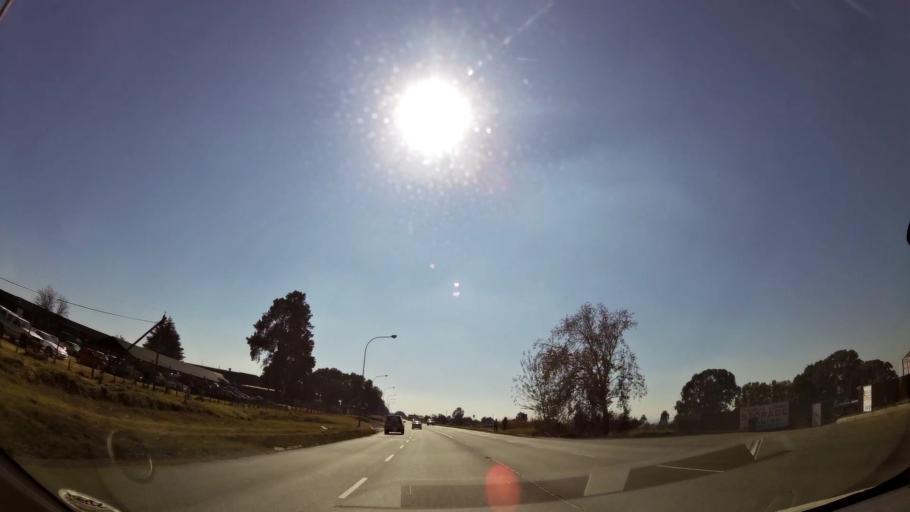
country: ZA
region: Mpumalanga
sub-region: Nkangala District Municipality
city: Witbank
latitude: -25.8552
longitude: 29.2323
